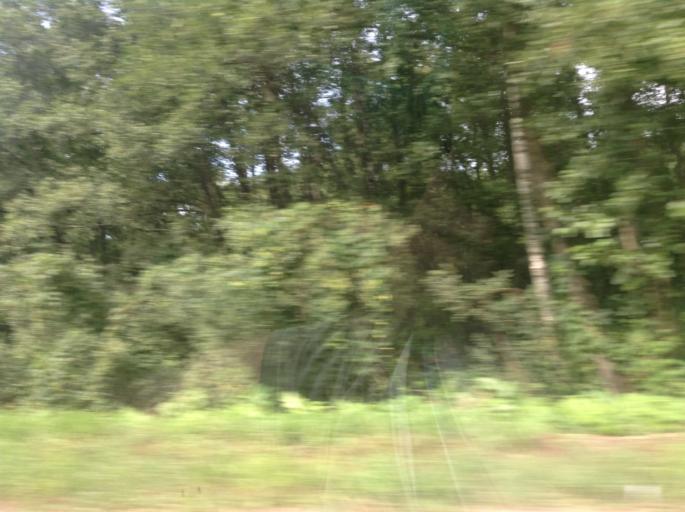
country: RU
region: Moskovskaya
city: Yegor'yevsk
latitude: 55.3606
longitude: 39.1059
